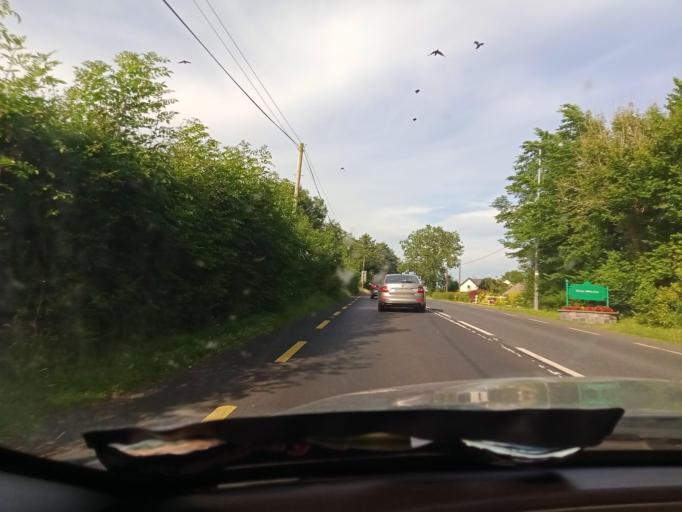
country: IE
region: Ulster
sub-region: An Cabhan
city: Cavan
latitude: 53.9378
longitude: -7.3986
